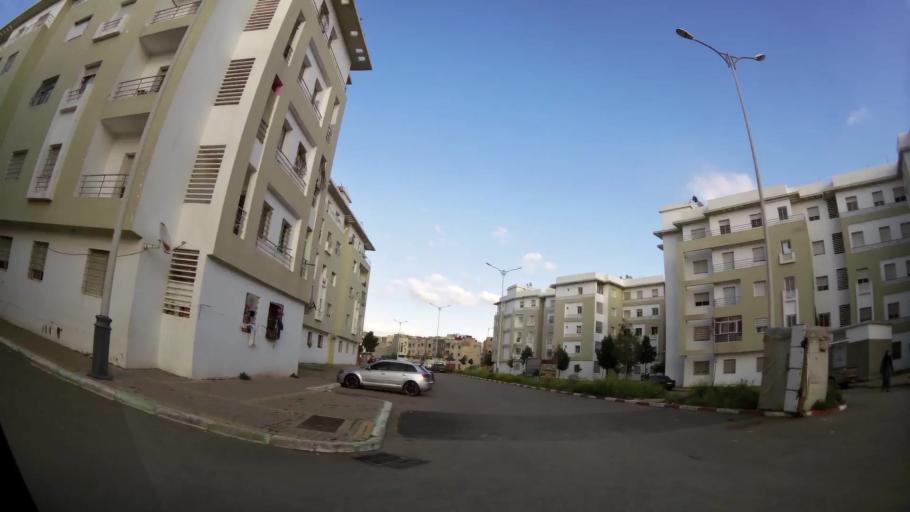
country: MA
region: Chaouia-Ouardigha
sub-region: Settat Province
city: Settat
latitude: 32.9977
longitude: -7.6335
